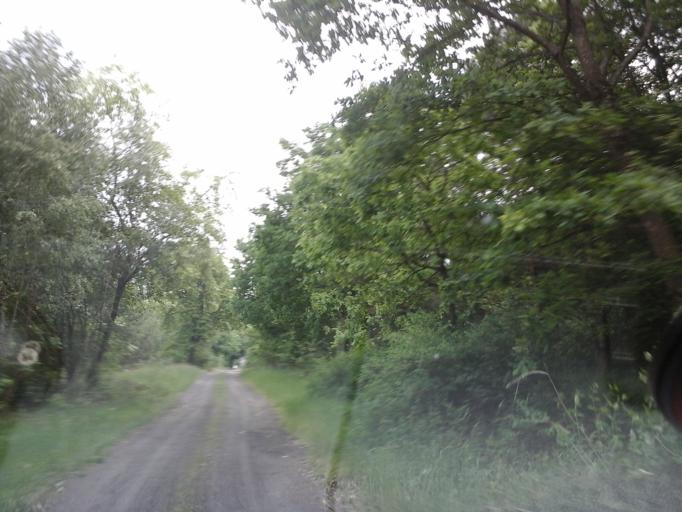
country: PL
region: West Pomeranian Voivodeship
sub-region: Powiat choszczenski
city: Bierzwnik
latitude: 53.1460
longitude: 15.6189
